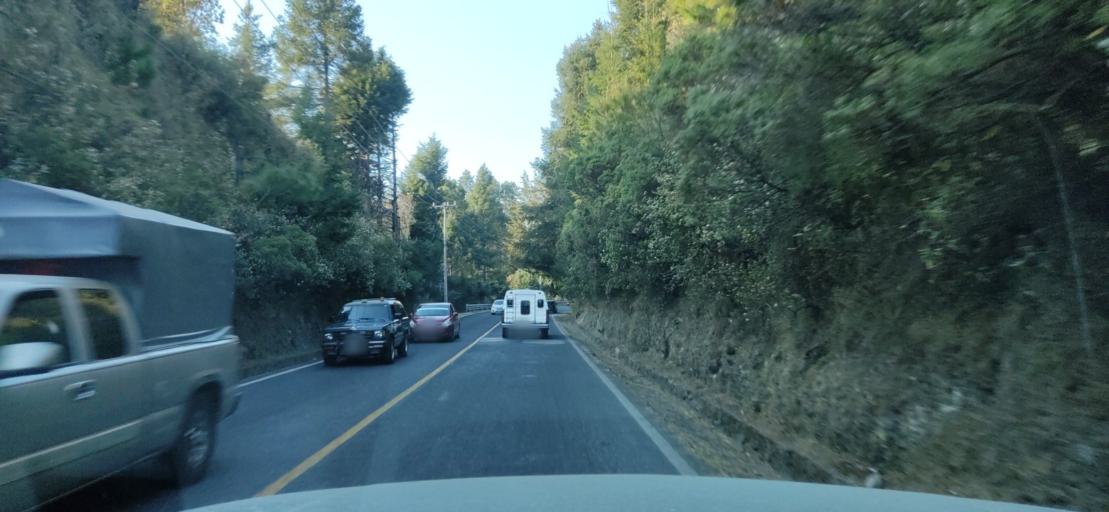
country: MX
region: Mexico
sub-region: Ocoyoacac
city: San Jeronimo Acazulco
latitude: 19.2567
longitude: -99.3783
